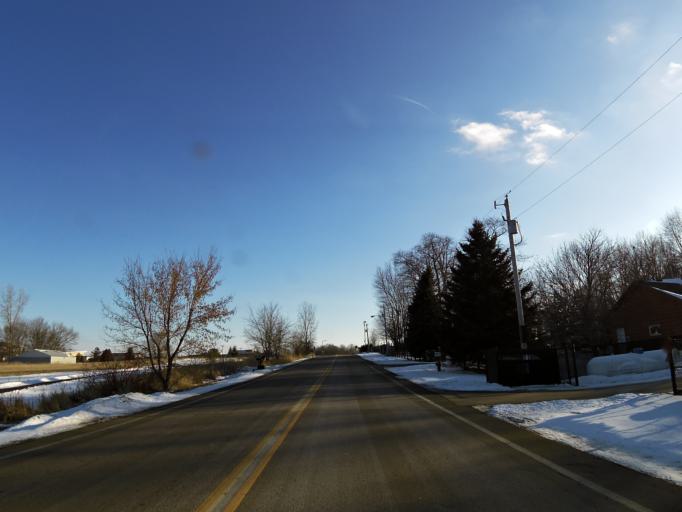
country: US
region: Minnesota
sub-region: Scott County
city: Prior Lake
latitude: 44.7522
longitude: -93.4496
